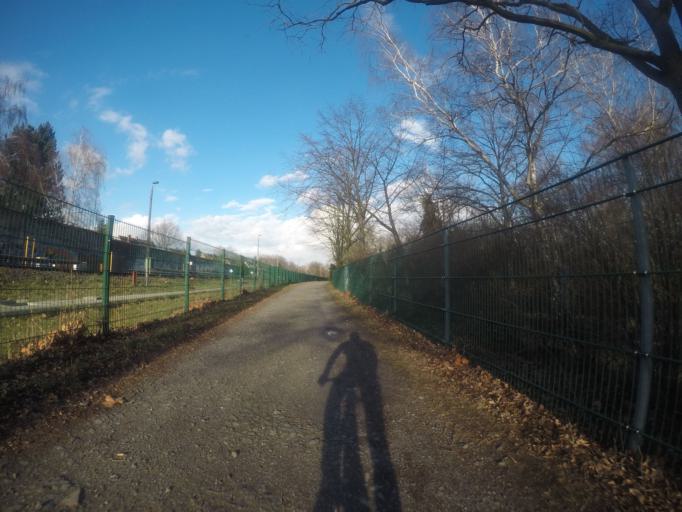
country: DE
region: Berlin
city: Biesdorf
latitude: 52.5104
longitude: 13.5681
